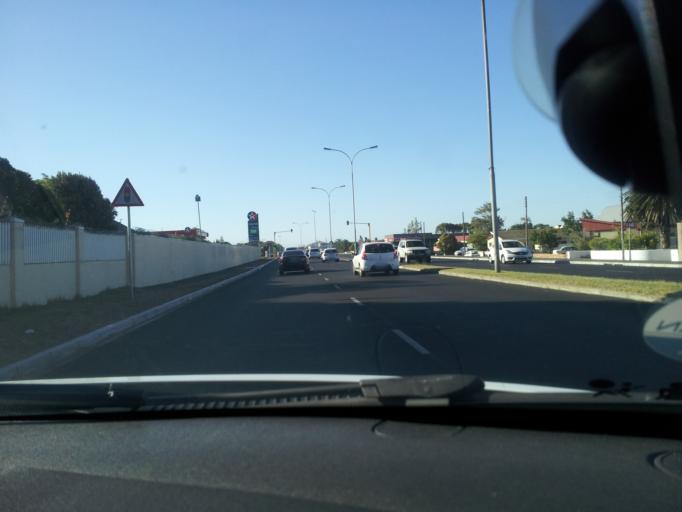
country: ZA
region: Western Cape
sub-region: Overberg District Municipality
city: Grabouw
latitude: -34.1306
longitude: 18.8427
